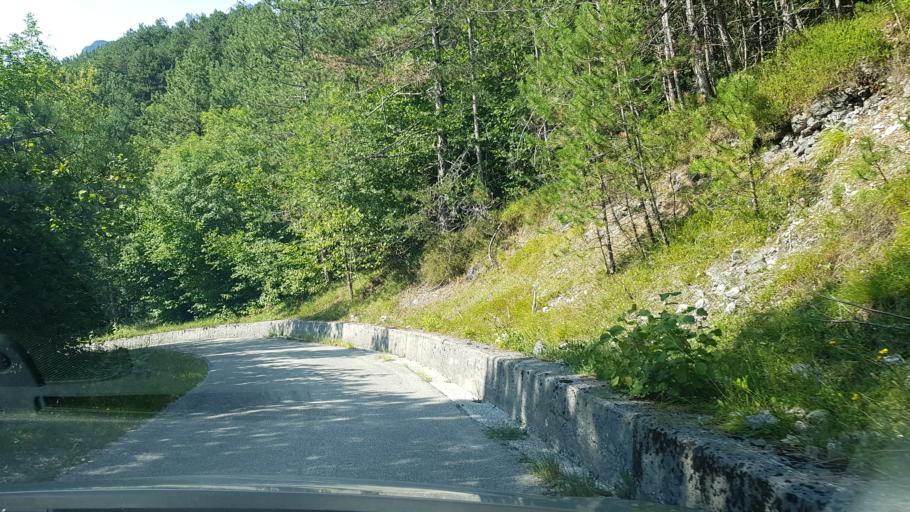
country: IT
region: Friuli Venezia Giulia
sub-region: Provincia di Udine
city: Moggio Udinese
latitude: 46.4356
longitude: 13.2054
